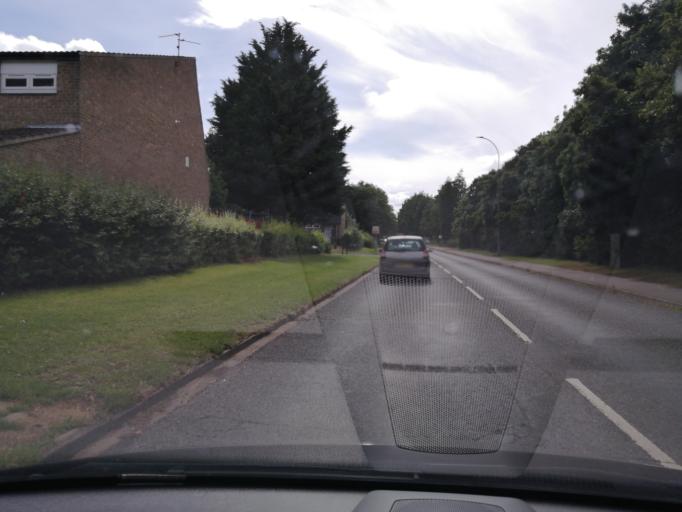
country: GB
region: England
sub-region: Cambridgeshire
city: Yaxley
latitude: 52.5461
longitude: -0.2898
